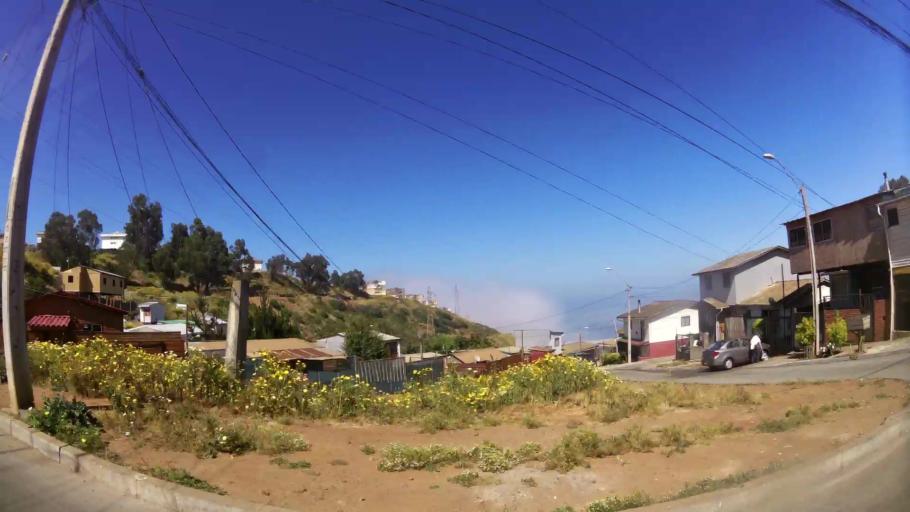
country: CL
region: Valparaiso
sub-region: Provincia de Valparaiso
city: Valparaiso
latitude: -33.0460
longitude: -71.6513
